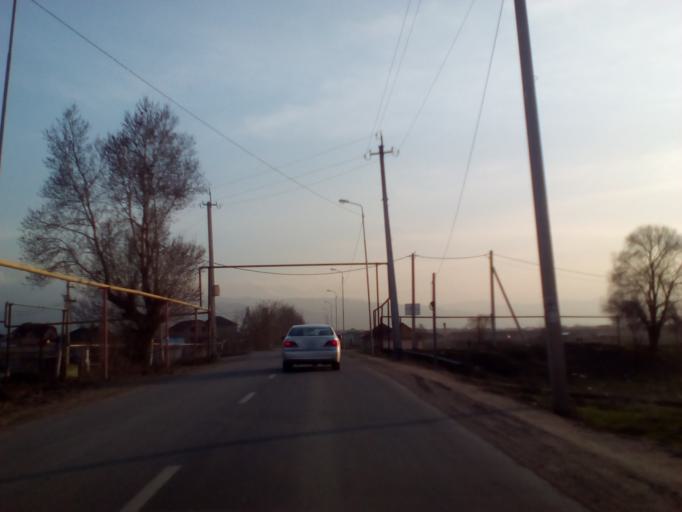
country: KZ
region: Almaty Oblysy
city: Burunday
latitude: 43.2389
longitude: 76.7444
